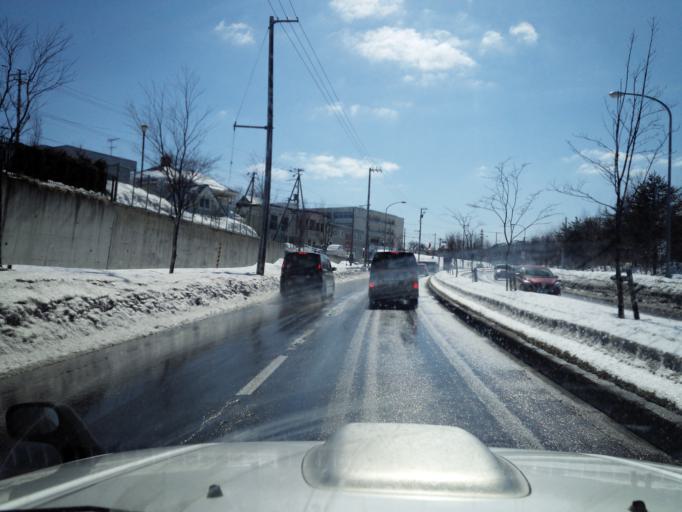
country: JP
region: Hokkaido
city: Kitahiroshima
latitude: 42.9992
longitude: 141.4611
